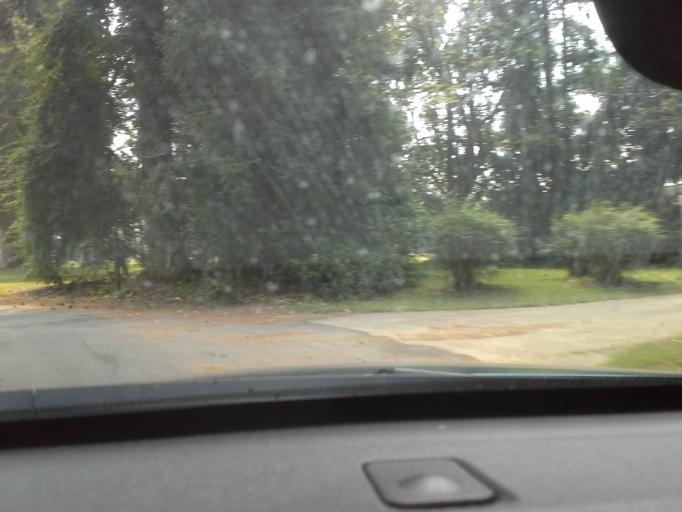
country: US
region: North Carolina
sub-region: Washington County
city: Plymouth
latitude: 35.8583
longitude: -76.7616
